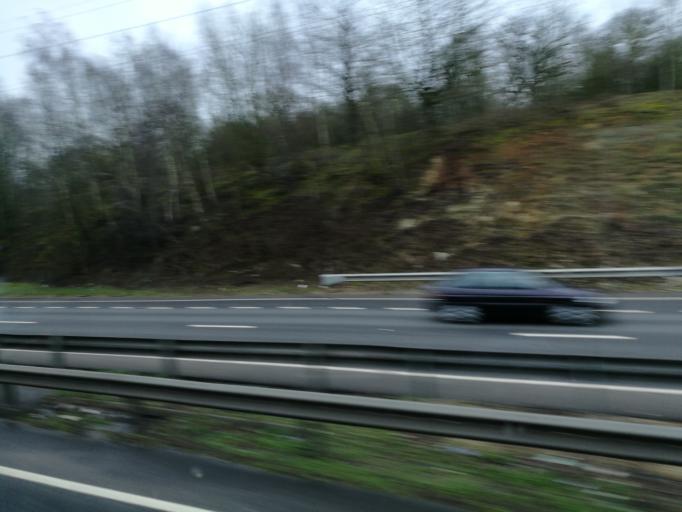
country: GB
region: England
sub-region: Luton
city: Luton
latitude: 51.8661
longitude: -0.4045
